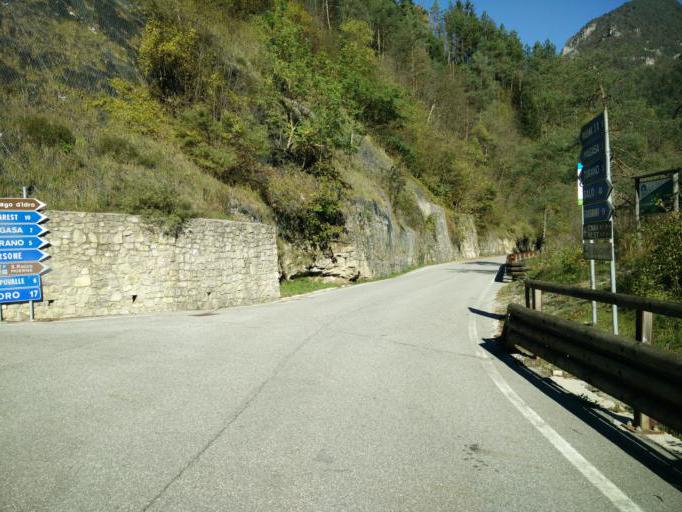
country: IT
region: Lombardy
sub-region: Provincia di Brescia
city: Valvestino
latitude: 45.7464
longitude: 10.5908
